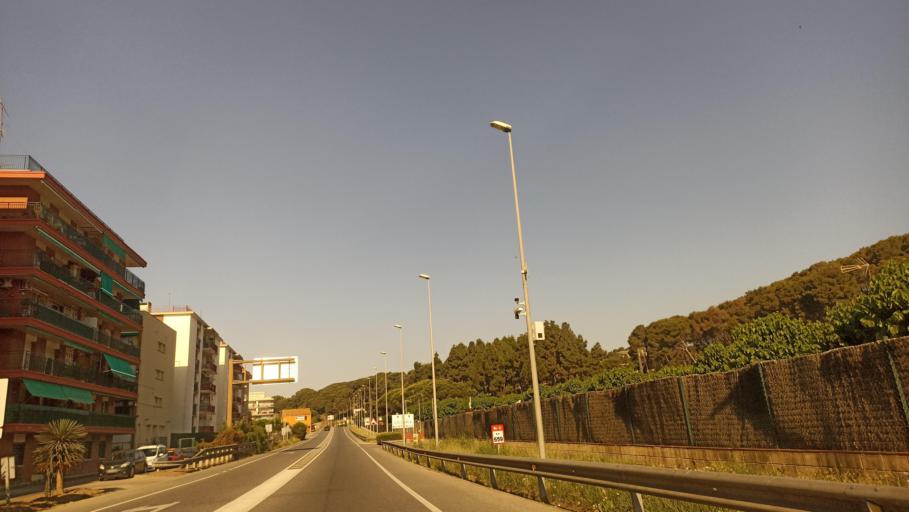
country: ES
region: Catalonia
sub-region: Provincia de Barcelona
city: Canet de Mar
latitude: 41.5852
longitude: 2.5740
